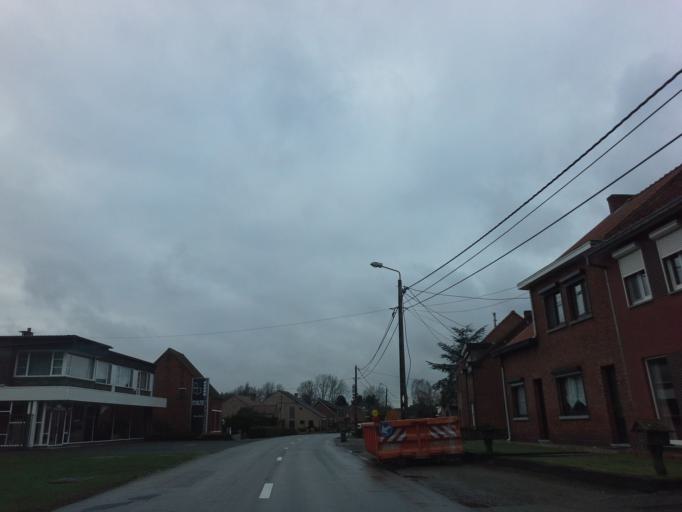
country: BE
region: Flanders
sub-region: Provincie Antwerpen
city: Mol
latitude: 51.1496
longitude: 5.1225
